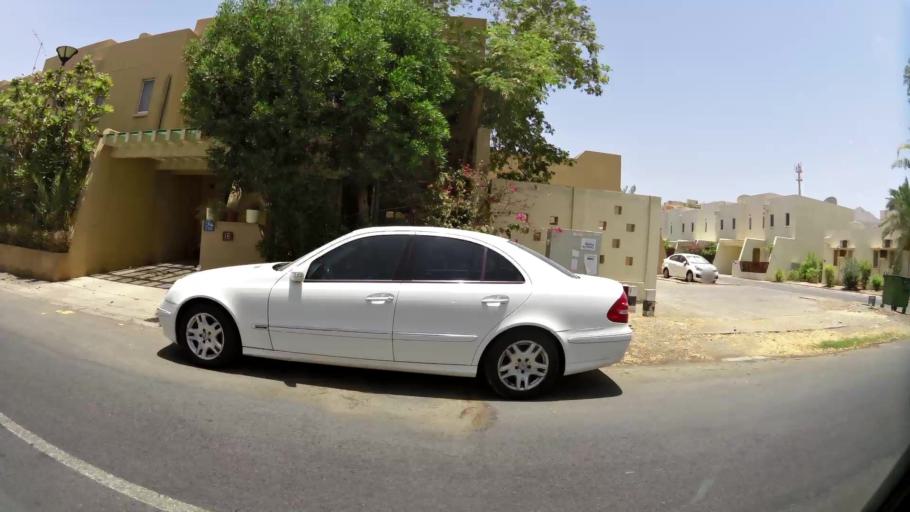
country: OM
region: Muhafazat Masqat
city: Bawshar
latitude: 23.5968
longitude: 58.4591
